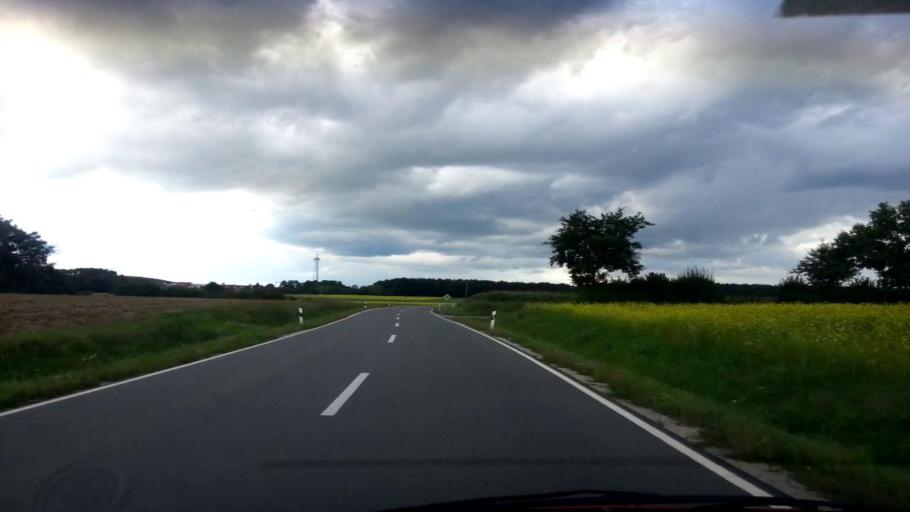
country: DE
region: Bavaria
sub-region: Regierungsbezirk Mittelfranken
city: Hemhofen
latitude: 49.6937
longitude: 10.9576
